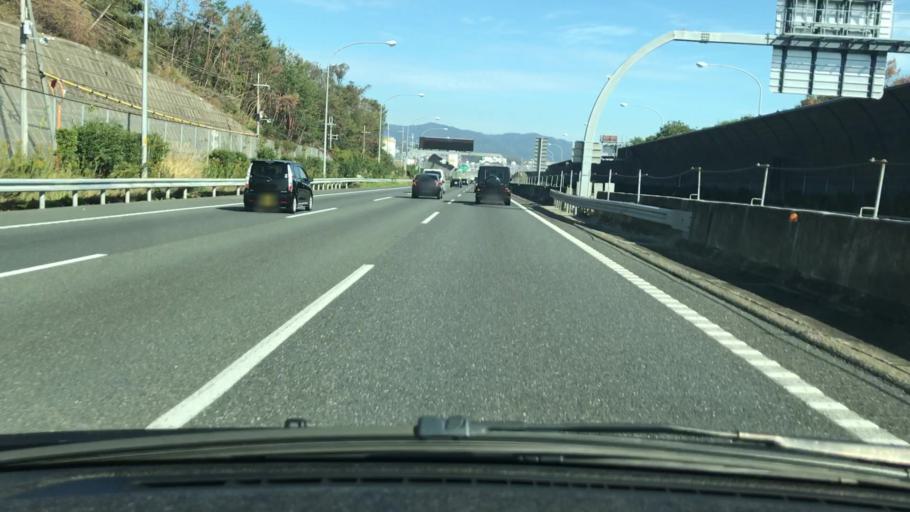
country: JP
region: Osaka
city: Ibaraki
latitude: 34.8251
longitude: 135.5554
